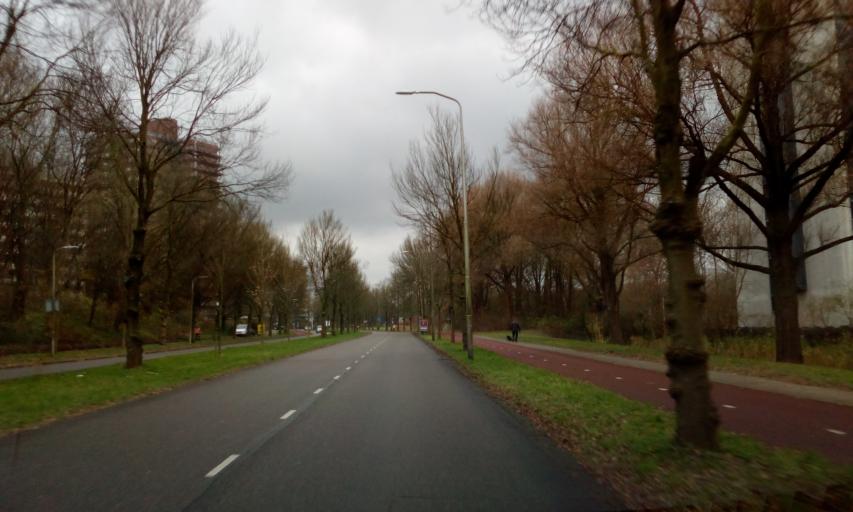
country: NL
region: South Holland
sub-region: Gemeente Zoetermeer
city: Zoetermeer
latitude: 52.0563
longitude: 4.4818
